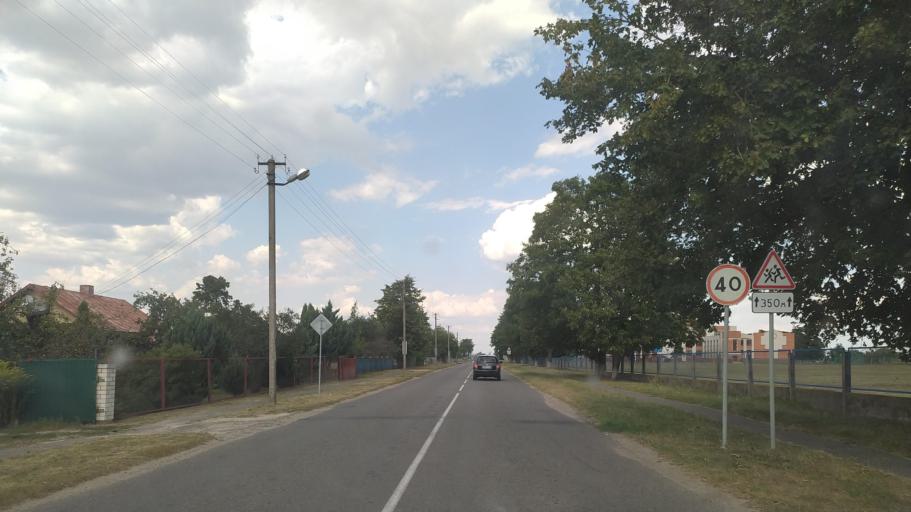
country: BY
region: Brest
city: Drahichyn
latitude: 52.1134
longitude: 25.1154
